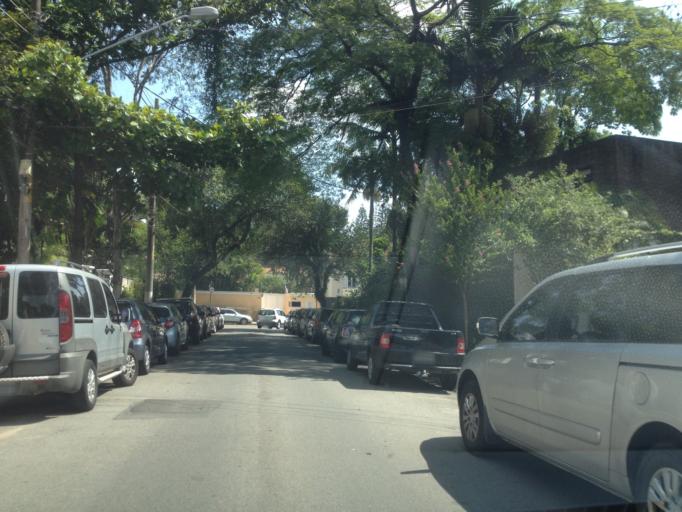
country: BR
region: Sao Paulo
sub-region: Sao Paulo
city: Sao Paulo
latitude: -23.5697
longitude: -46.6789
